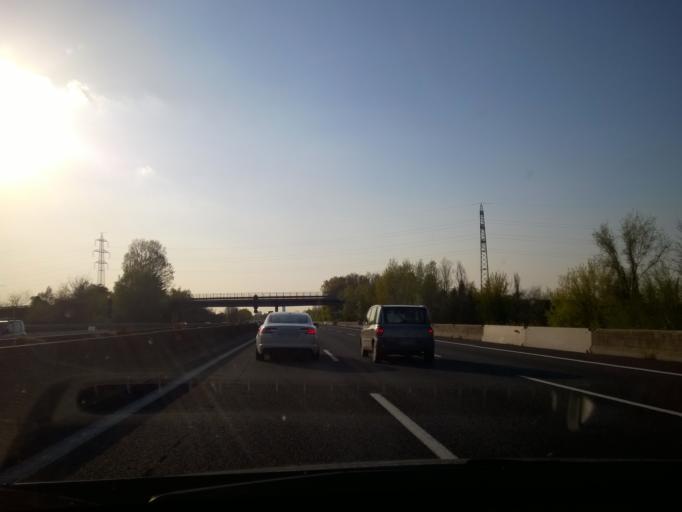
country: IT
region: Emilia-Romagna
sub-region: Provincia di Bologna
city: Villanova
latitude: 44.4793
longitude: 11.4487
